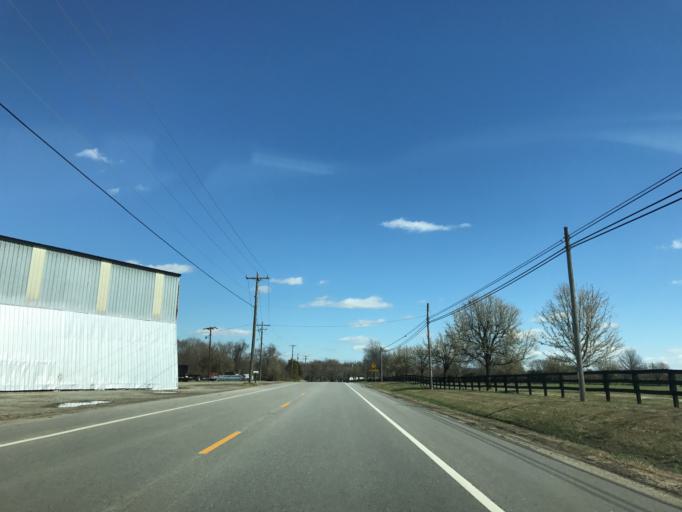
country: US
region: Maryland
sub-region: Queen Anne's County
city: Kingstown
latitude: 39.2515
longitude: -75.8523
